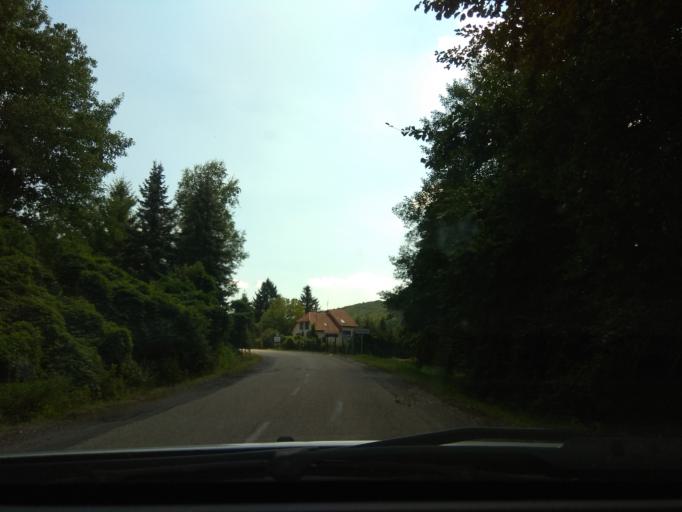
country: HU
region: Borsod-Abauj-Zemplen
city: Harsany
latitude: 47.9944
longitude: 20.7625
